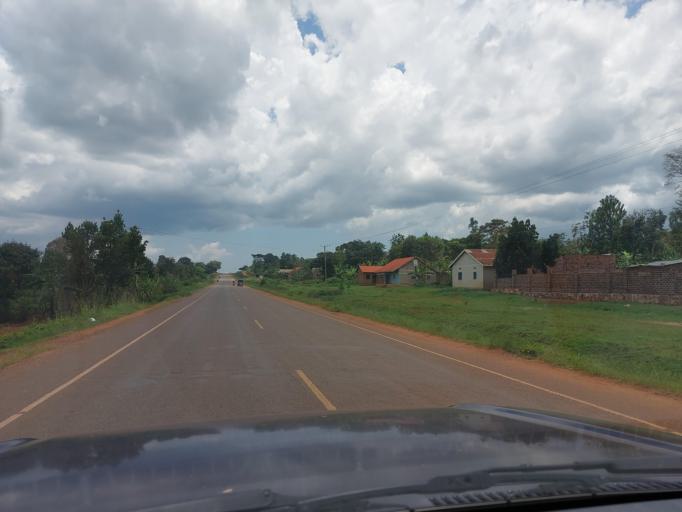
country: UG
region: Central Region
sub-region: Mukono District
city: Mukono
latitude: 0.2903
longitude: 32.7876
